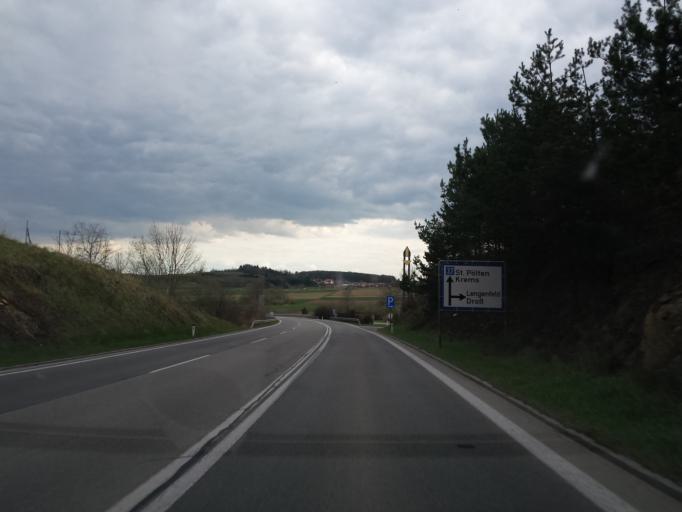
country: AT
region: Lower Austria
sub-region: Politischer Bezirk Krems
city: Lengenfeld
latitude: 48.4739
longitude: 15.5795
